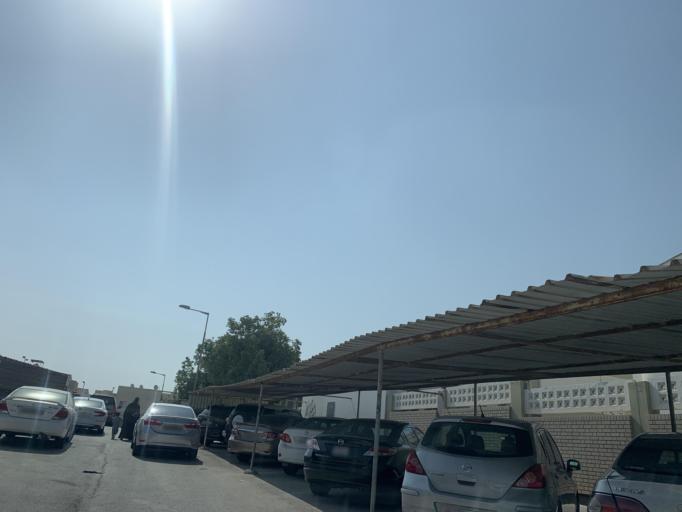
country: BH
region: Central Governorate
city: Madinat Hamad
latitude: 26.1330
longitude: 50.5031
